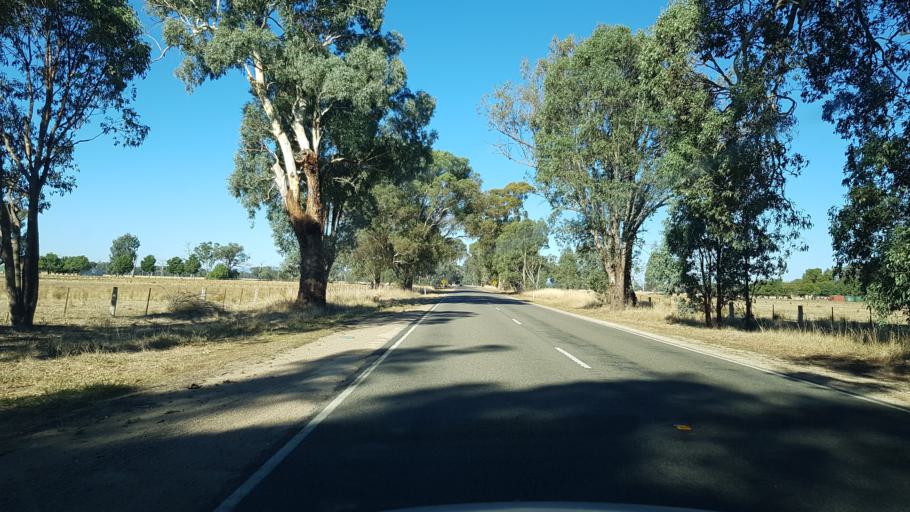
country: AU
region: Victoria
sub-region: Wangaratta
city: Wangaratta
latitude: -36.4354
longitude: 146.3202
